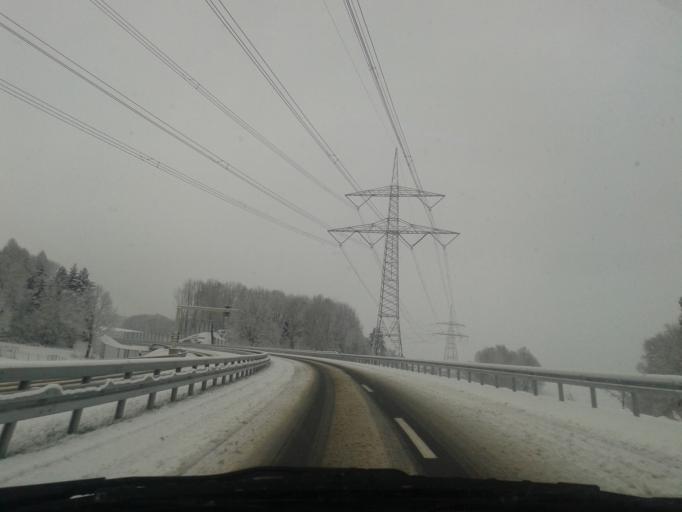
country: DE
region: Saxony
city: Lohmen
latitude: 51.0044
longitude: 13.9591
